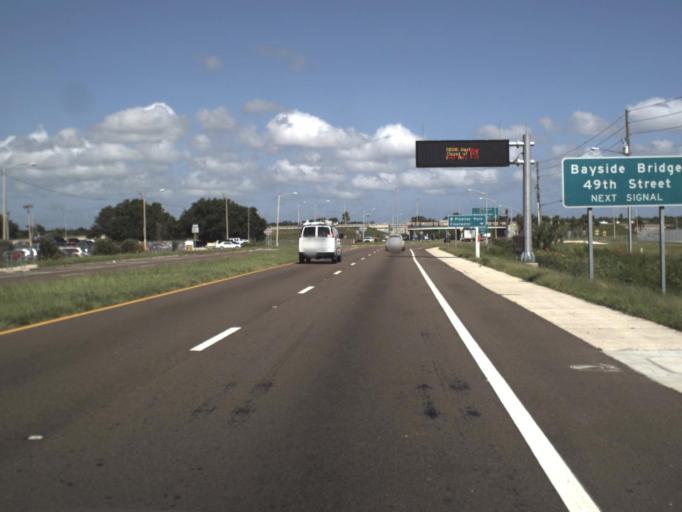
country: US
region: Florida
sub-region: Pinellas County
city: South Highpoint
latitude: 27.9074
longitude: -82.6974
